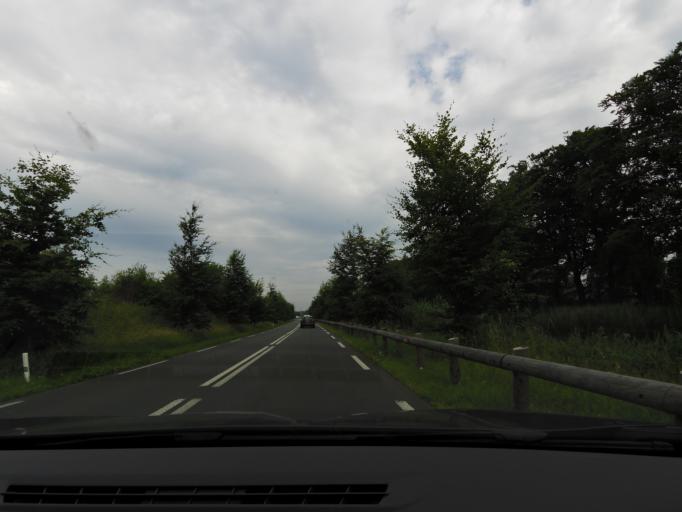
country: NL
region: Gelderland
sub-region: Gemeente Rheden
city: Dieren
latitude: 52.0647
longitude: 6.0981
